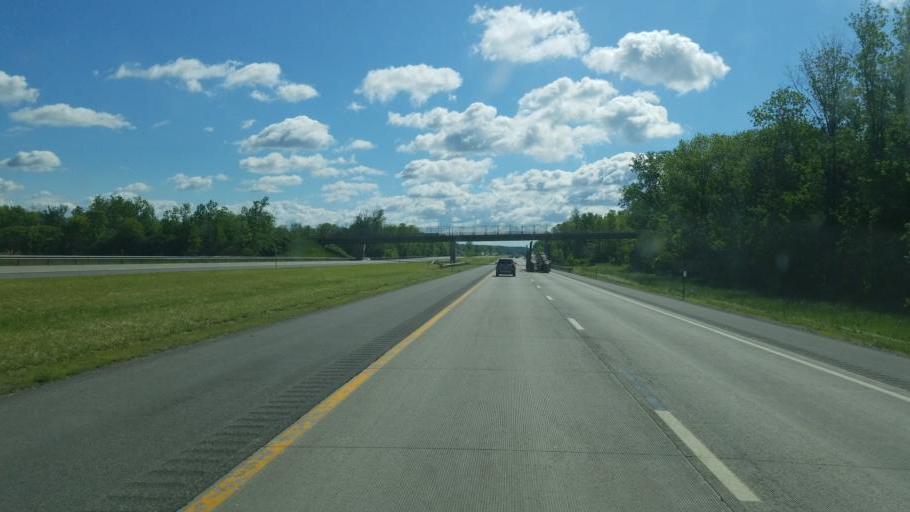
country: US
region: New York
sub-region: Onondaga County
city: Peru
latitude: 43.0863
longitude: -76.4116
